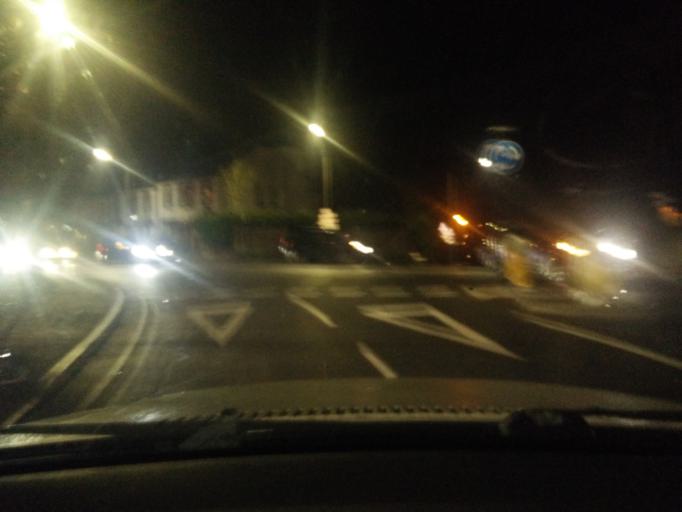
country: GB
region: England
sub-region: Buckinghamshire
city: Amersham on the Hill
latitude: 51.6759
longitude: -0.6090
